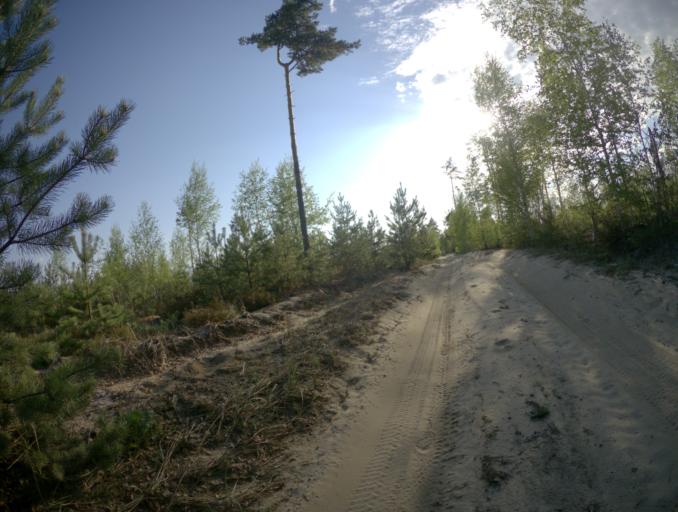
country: RU
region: Vladimir
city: Vyazniki
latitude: 56.4051
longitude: 42.1817
